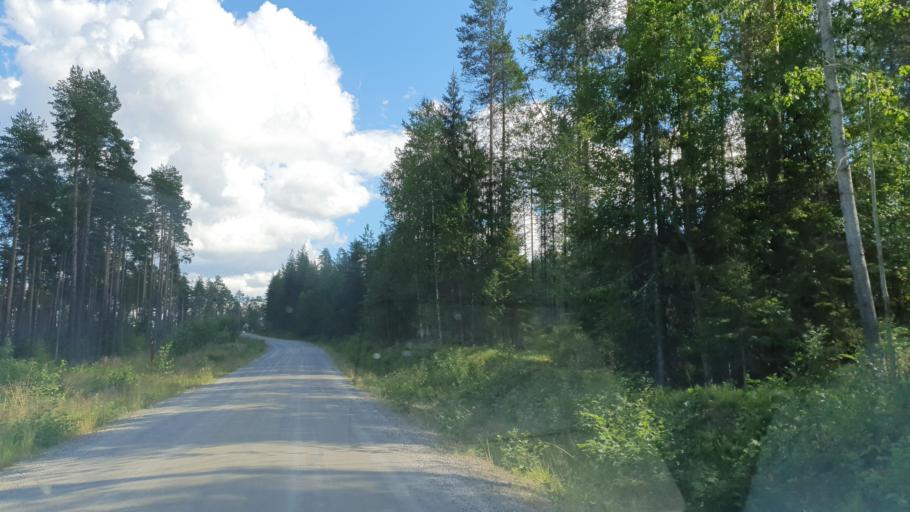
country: FI
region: Kainuu
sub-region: Kehys-Kainuu
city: Kuhmo
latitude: 64.0983
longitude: 29.4071
